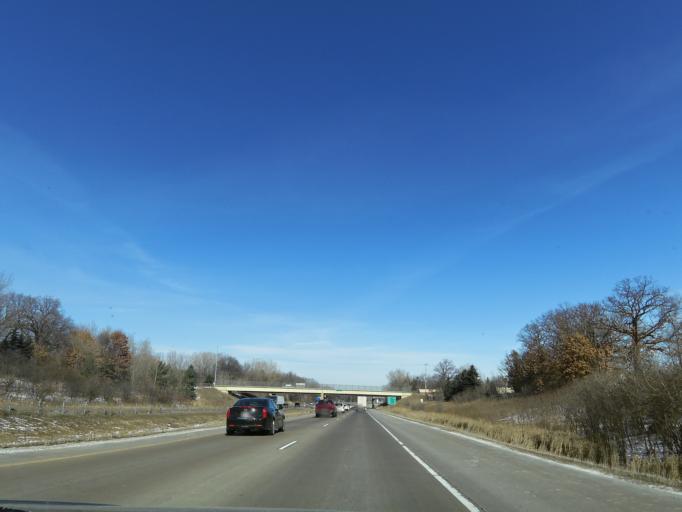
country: US
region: Minnesota
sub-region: Washington County
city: Oakdale
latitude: 44.9856
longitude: -92.9602
